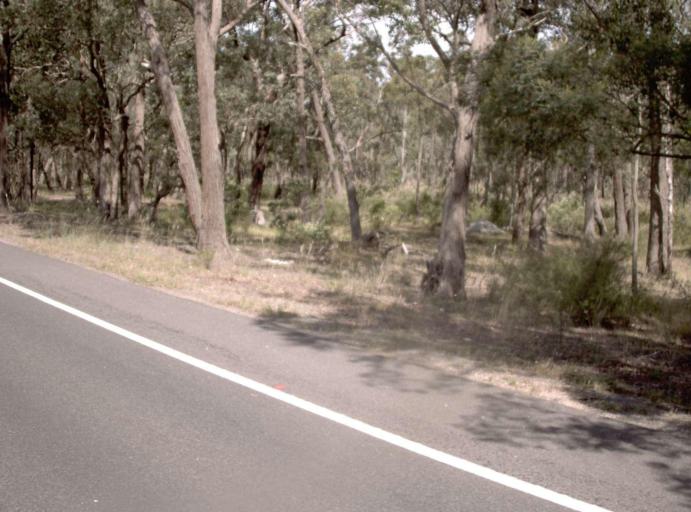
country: AU
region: Victoria
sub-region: Wellington
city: Sale
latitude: -37.9206
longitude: 147.2550
